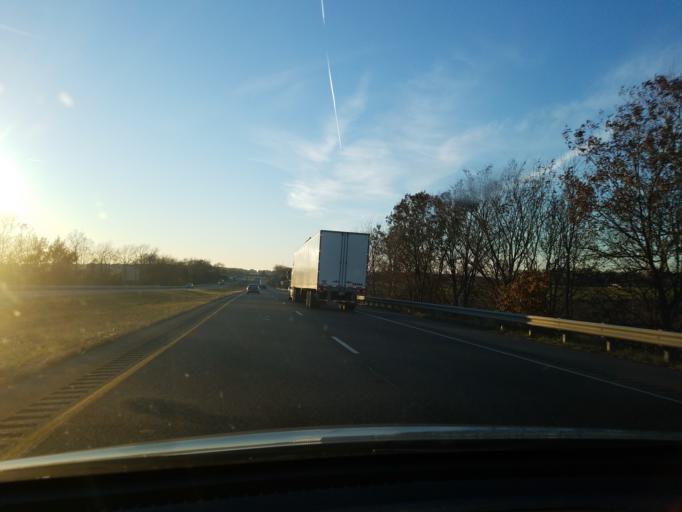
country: US
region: Indiana
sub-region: Gibson County
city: Haubstadt
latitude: 38.1671
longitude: -87.5664
